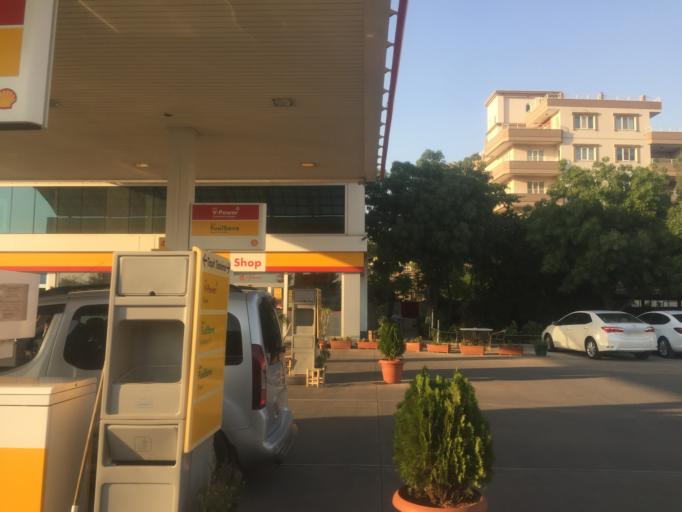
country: TR
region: Mardin
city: Midyat
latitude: 37.4211
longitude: 41.3500
